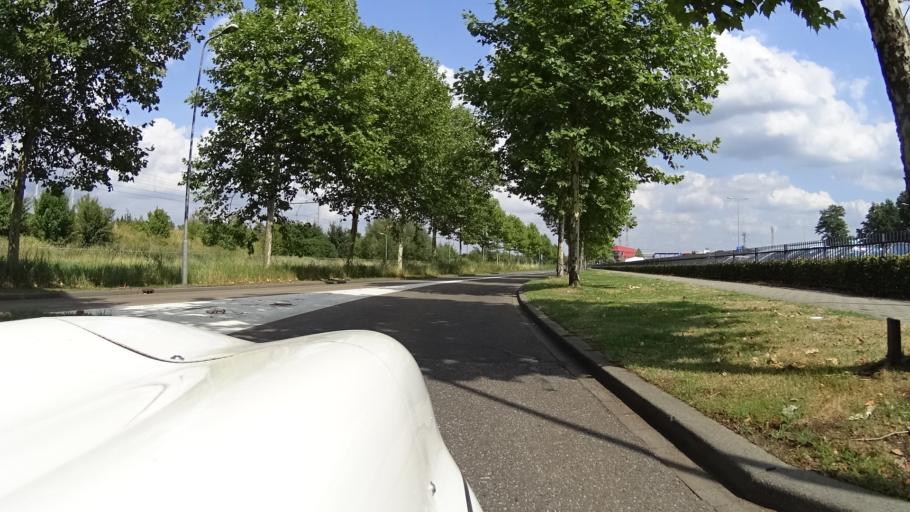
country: NL
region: North Brabant
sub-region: Gemeente 's-Hertogenbosch
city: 's-Hertogenbosch
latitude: 51.7003
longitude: 5.3223
